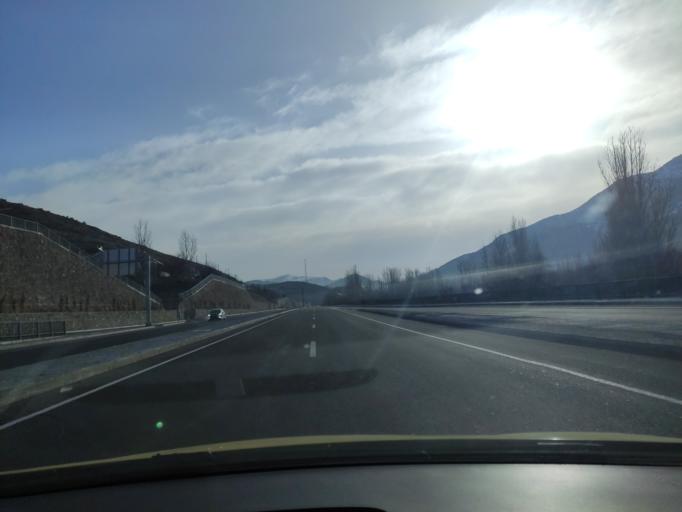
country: TR
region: Gumushane
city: Kale
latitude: 40.4051
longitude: 39.6110
